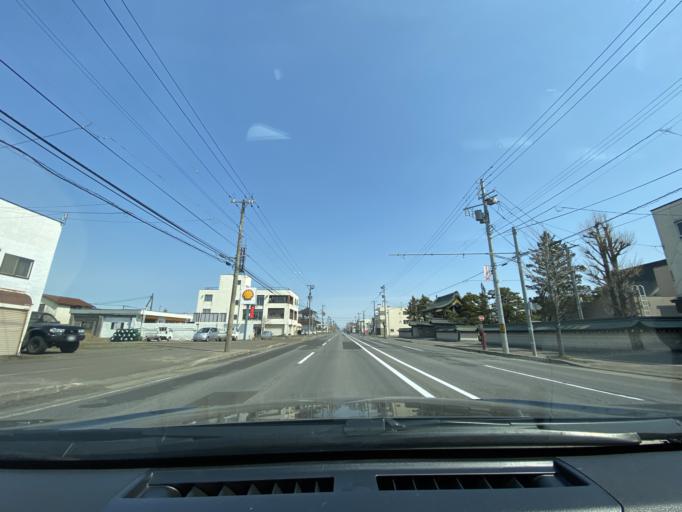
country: JP
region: Hokkaido
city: Bibai
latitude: 43.3257
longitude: 141.8585
